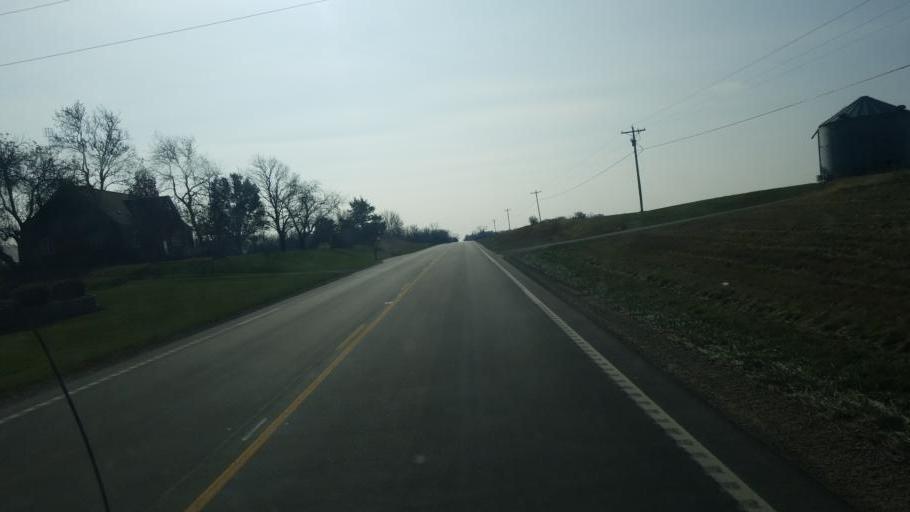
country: US
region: Ohio
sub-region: Mercer County
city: Fort Recovery
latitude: 40.4568
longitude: -84.7844
